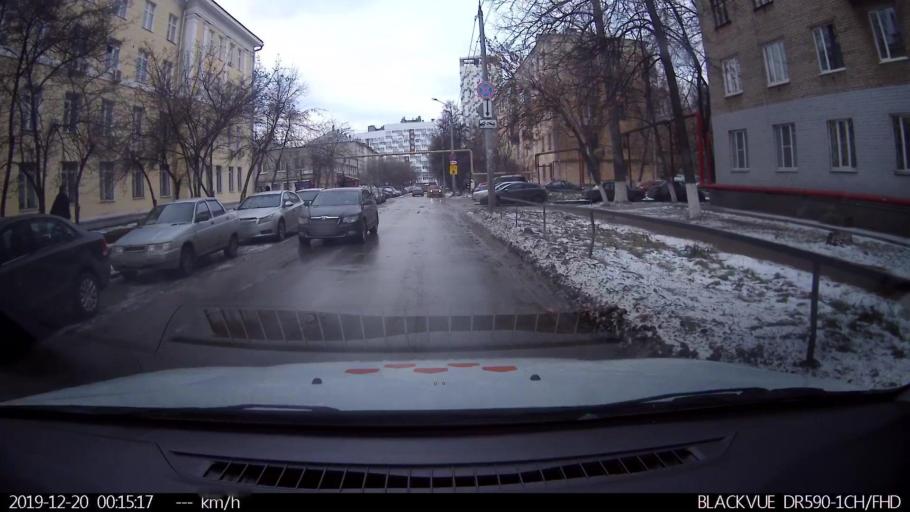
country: RU
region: Jaroslavl
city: Porech'ye-Rybnoye
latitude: 56.9949
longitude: 39.3869
